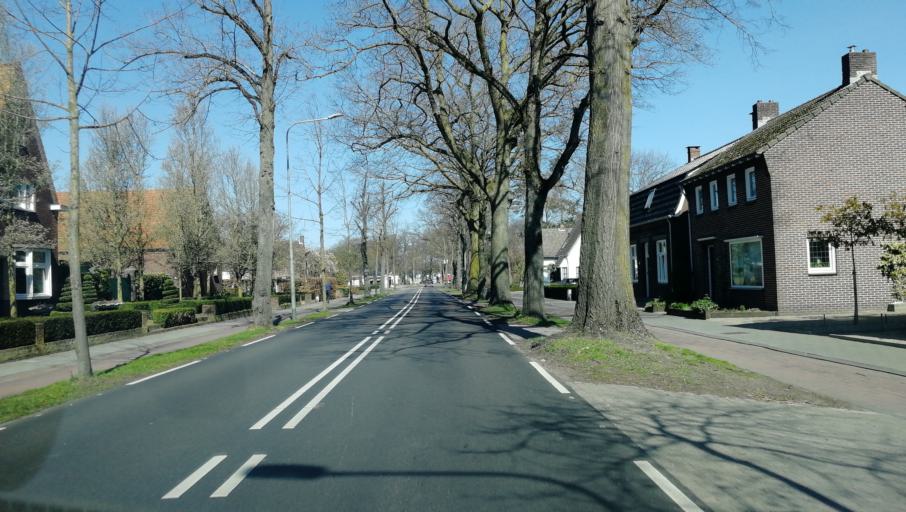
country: NL
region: Limburg
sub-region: Gemeente Venray
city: Venray
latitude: 51.4626
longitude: 6.0536
